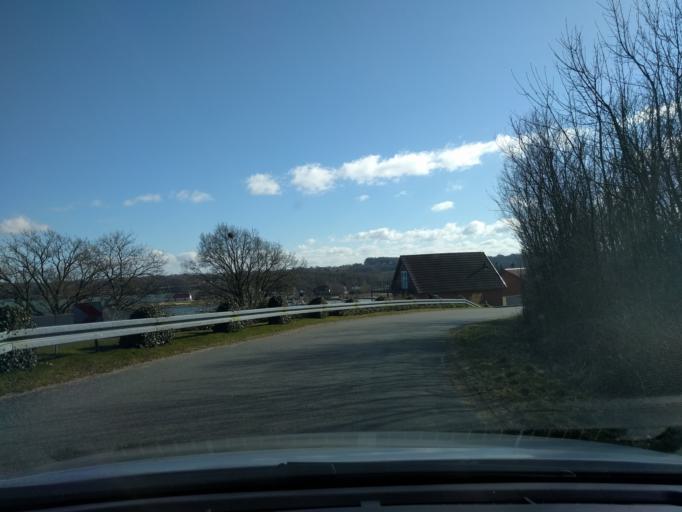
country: DK
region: South Denmark
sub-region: Aabenraa Kommune
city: Lojt Kirkeby
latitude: 55.1252
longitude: 9.4634
